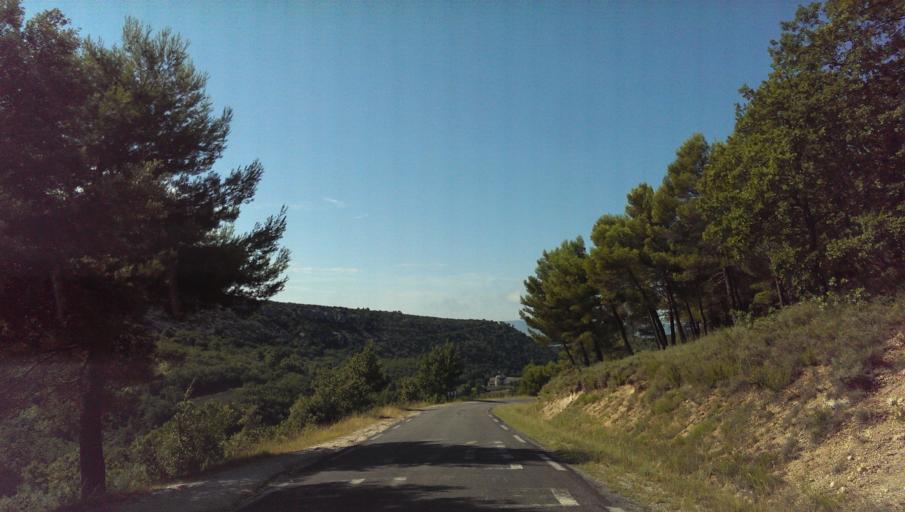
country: FR
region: Provence-Alpes-Cote d'Azur
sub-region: Departement du Vaucluse
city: Gordes
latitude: 43.9379
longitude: 5.1897
